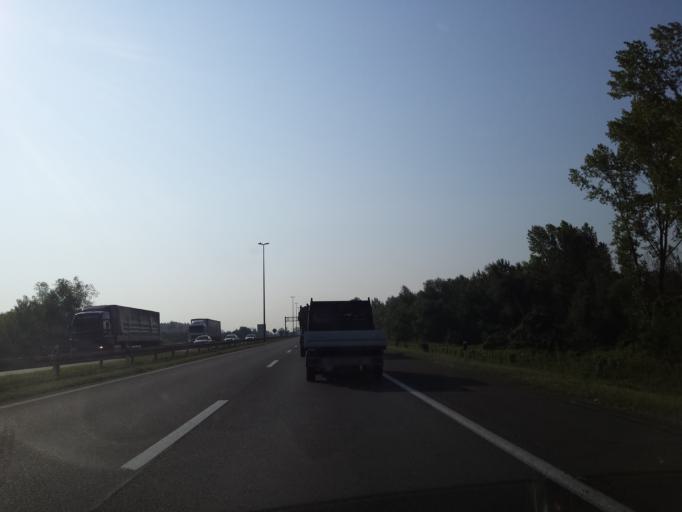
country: HR
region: Grad Zagreb
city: Jezdovec
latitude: 45.7833
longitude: 15.8627
